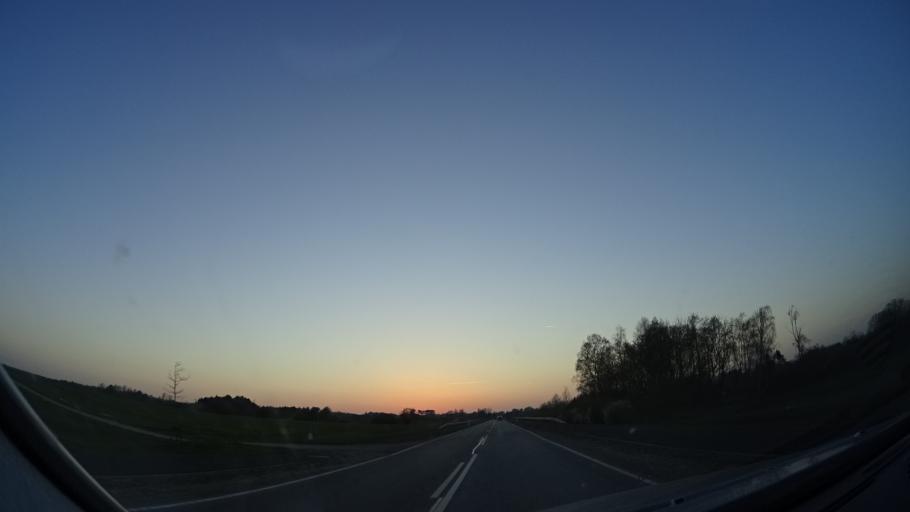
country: DK
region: Zealand
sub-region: Lejre Kommune
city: Ejby
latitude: 55.6656
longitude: 11.8955
